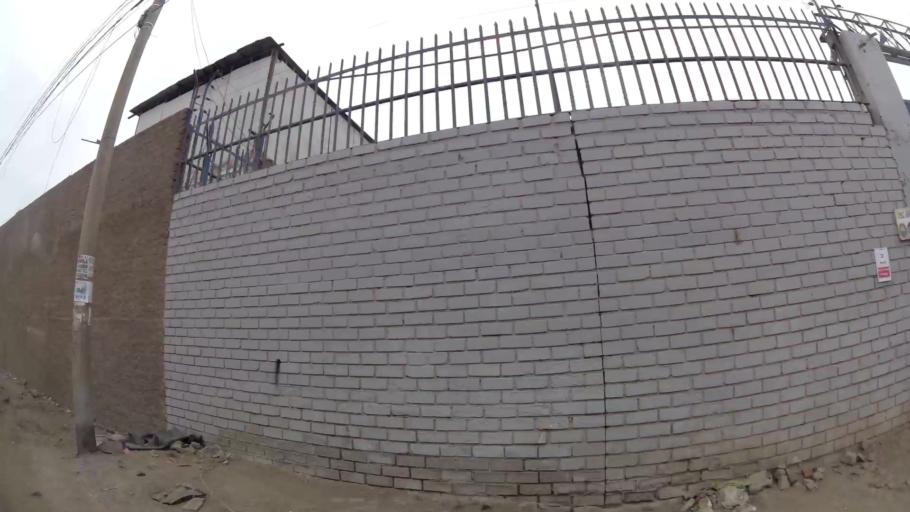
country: PE
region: Lima
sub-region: Lima
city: Surco
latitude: -12.2033
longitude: -76.9716
